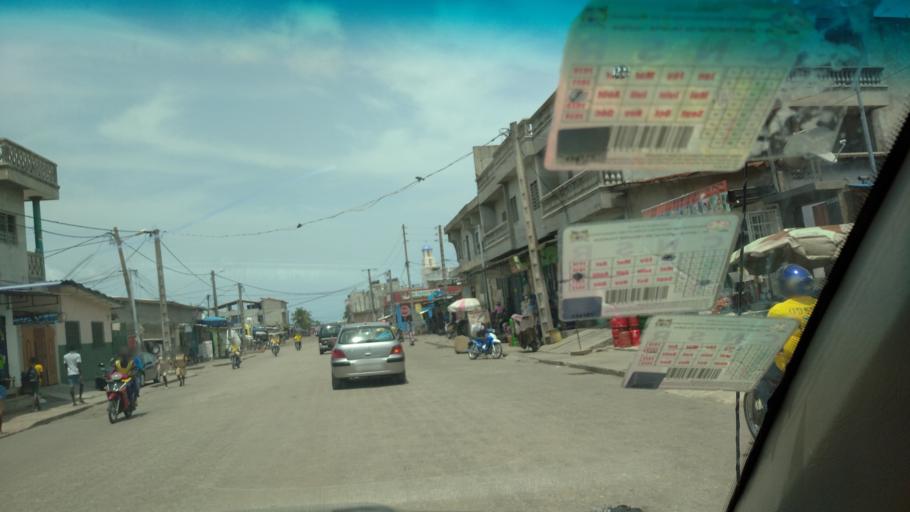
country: BJ
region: Littoral
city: Cotonou
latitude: 6.3901
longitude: 2.4616
